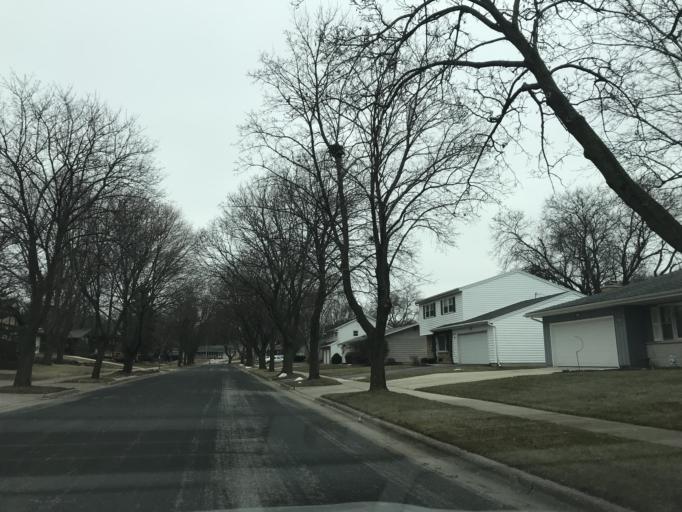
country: US
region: Wisconsin
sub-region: Dane County
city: Monona
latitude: 43.0869
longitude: -89.2966
